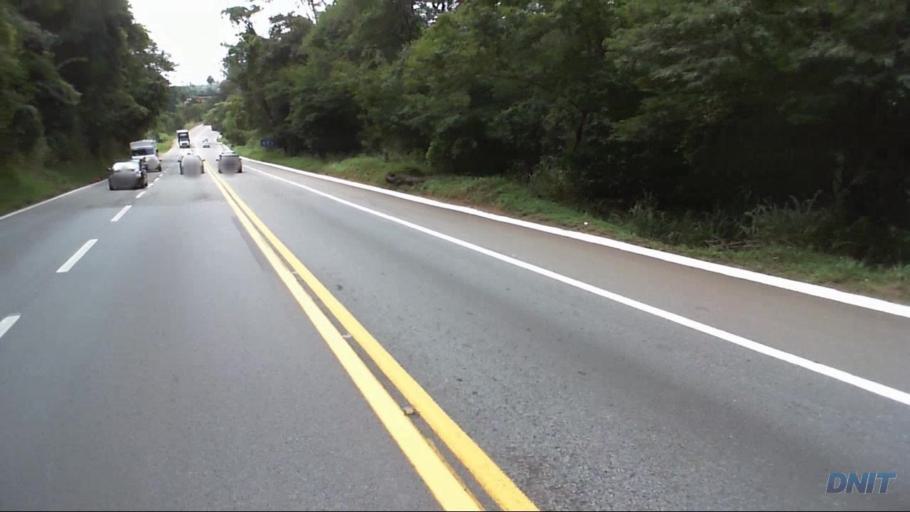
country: BR
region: Minas Gerais
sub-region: Santa Luzia
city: Santa Luzia
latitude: -19.7966
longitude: -43.7480
